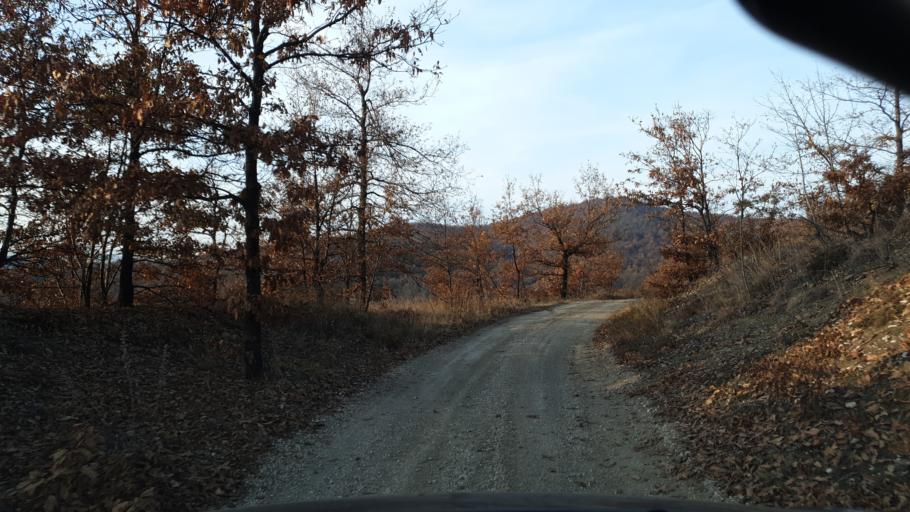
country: RS
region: Central Serbia
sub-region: Borski Okrug
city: Bor
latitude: 44.0688
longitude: 22.0745
